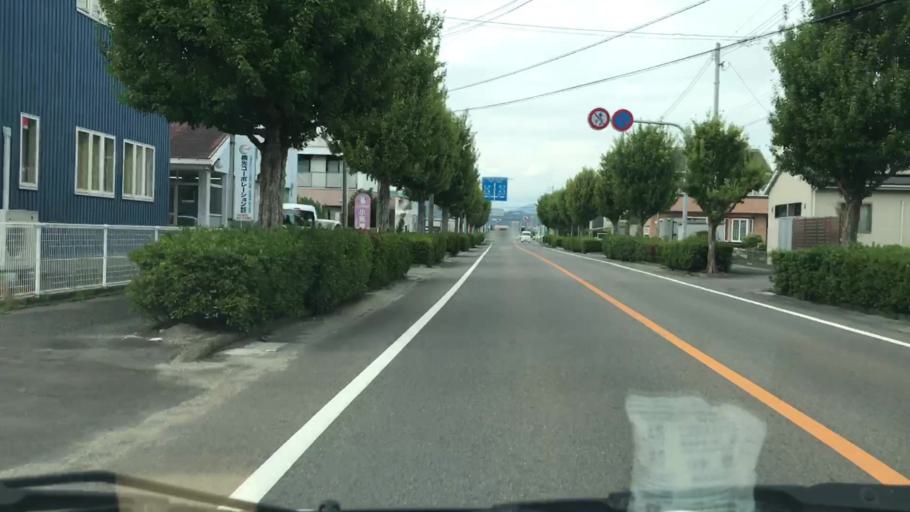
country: JP
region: Saga Prefecture
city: Saga-shi
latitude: 33.2668
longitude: 130.2621
